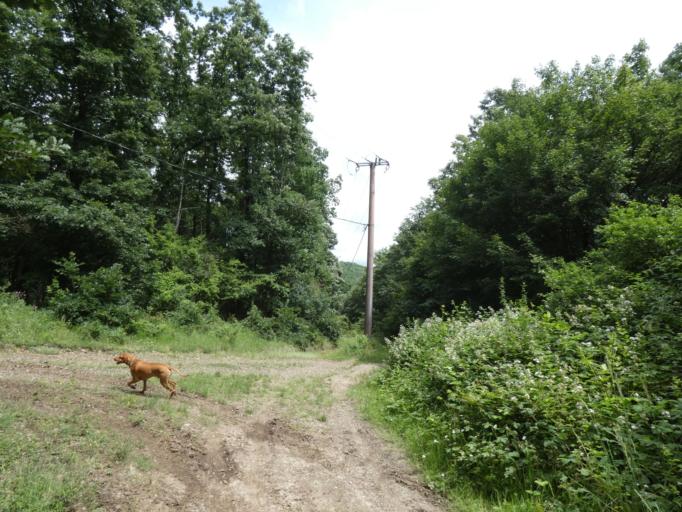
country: HU
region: Pest
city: Kismaros
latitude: 47.8467
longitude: 18.9761
